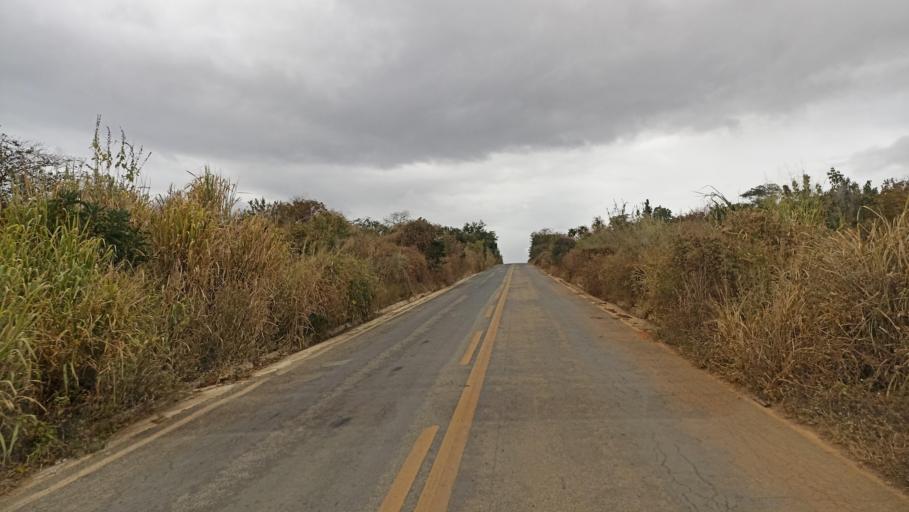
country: BR
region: Minas Gerais
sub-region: Itinga
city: Itinga
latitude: -16.6551
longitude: -41.8316
